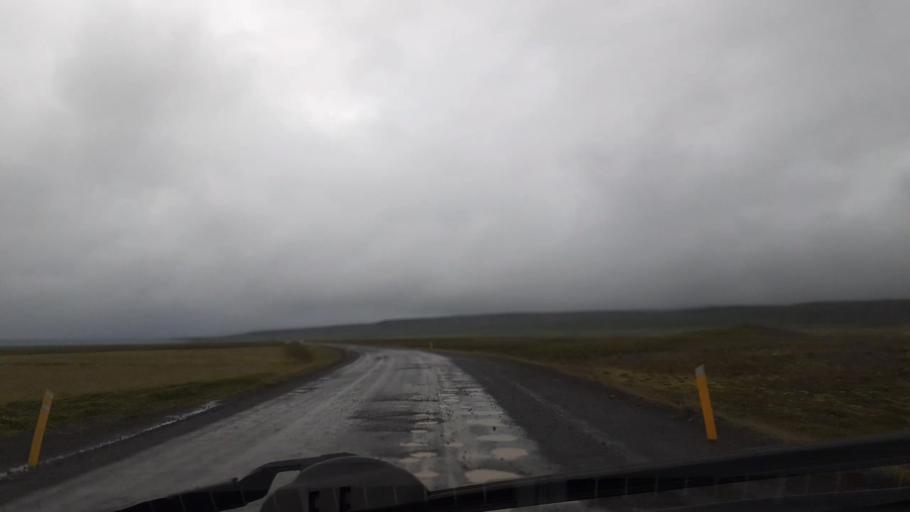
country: IS
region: East
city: Egilsstadir
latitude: 66.0334
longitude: -15.0555
